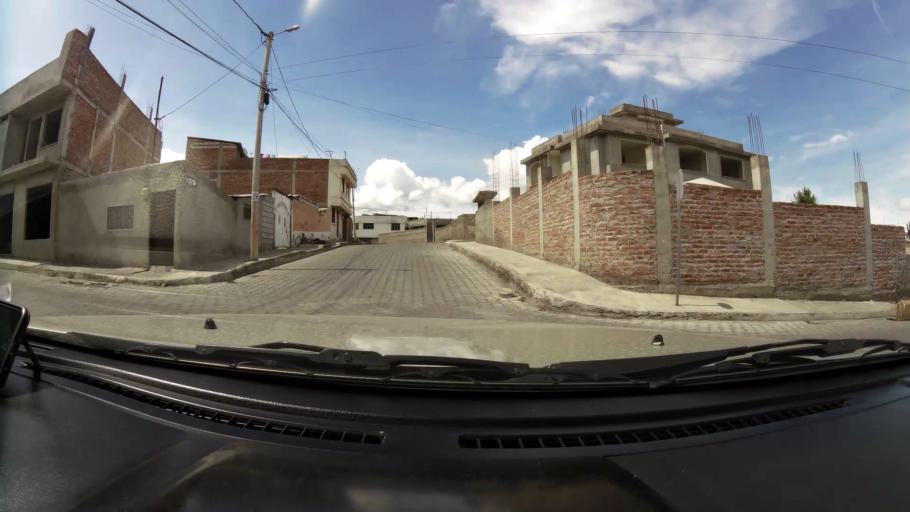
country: EC
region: Chimborazo
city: Riobamba
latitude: -1.6571
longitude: -78.6412
